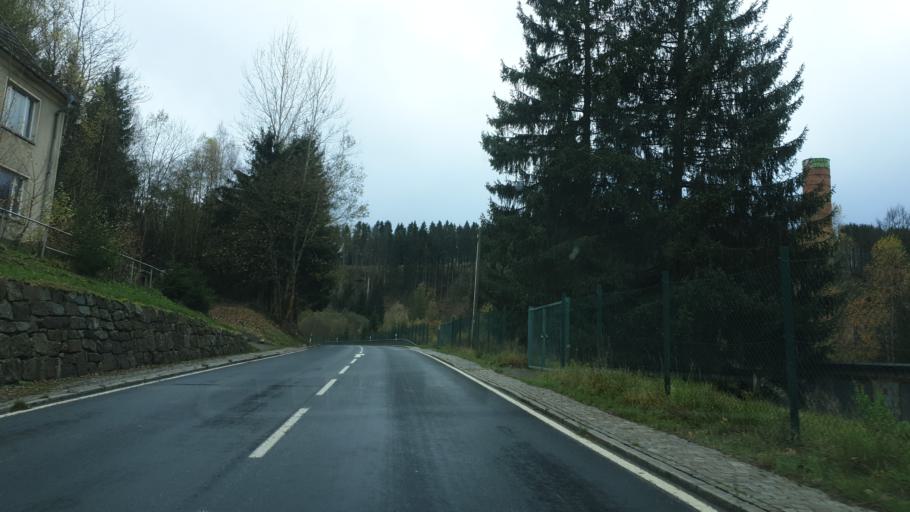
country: DE
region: Saxony
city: Schoenheide
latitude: 50.4943
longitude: 12.5460
